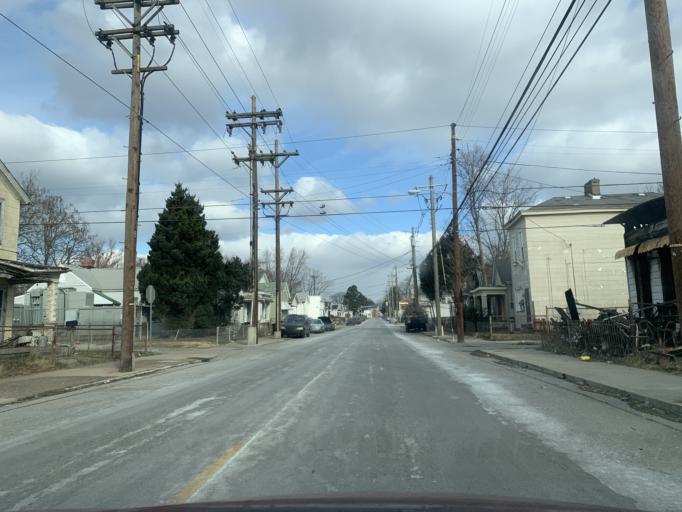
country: US
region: Kentucky
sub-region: Jefferson County
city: Louisville
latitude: 38.2612
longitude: -85.7935
